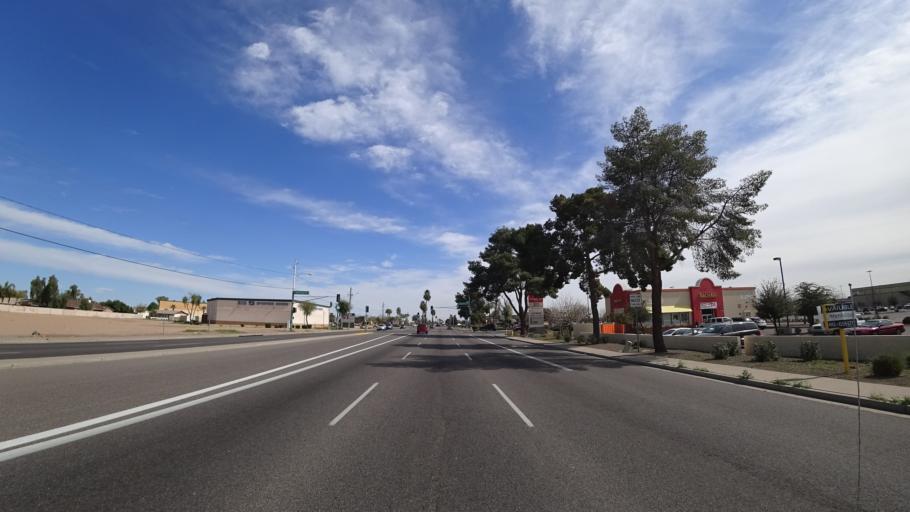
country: US
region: Arizona
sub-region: Maricopa County
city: Tolleson
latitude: 33.4800
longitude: -112.2259
